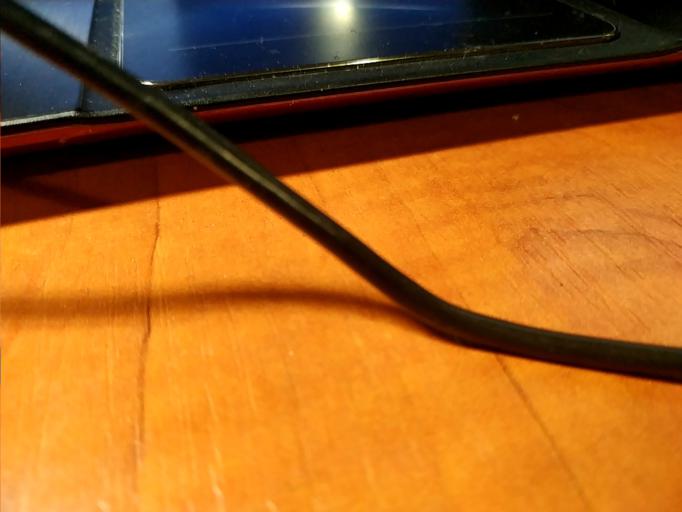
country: RU
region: Tverskaya
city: Vasil'yevskiy Mokh
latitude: 56.9463
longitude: 35.8938
